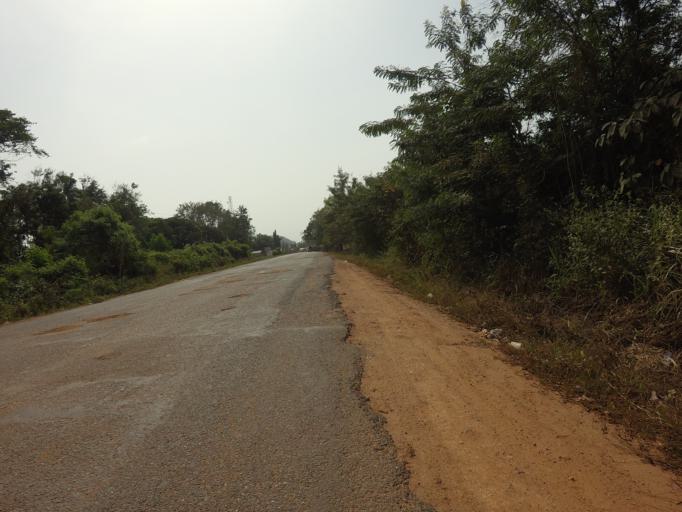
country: GH
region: Volta
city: Ho
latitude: 6.3799
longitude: 0.1869
